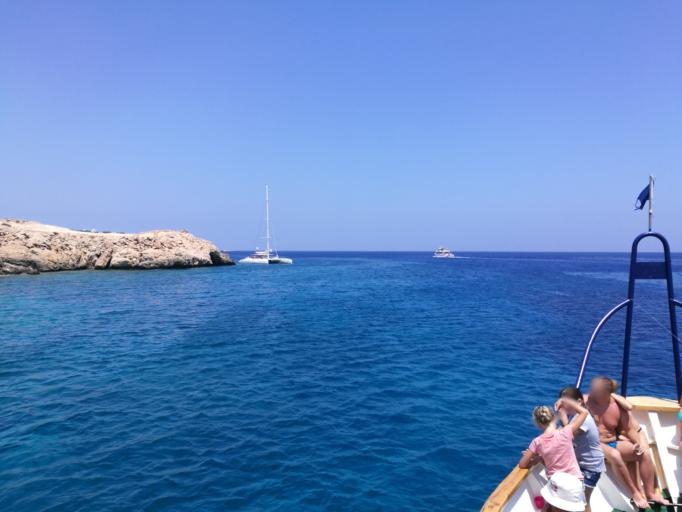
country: CY
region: Ammochostos
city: Protaras
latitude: 34.9722
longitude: 34.0768
